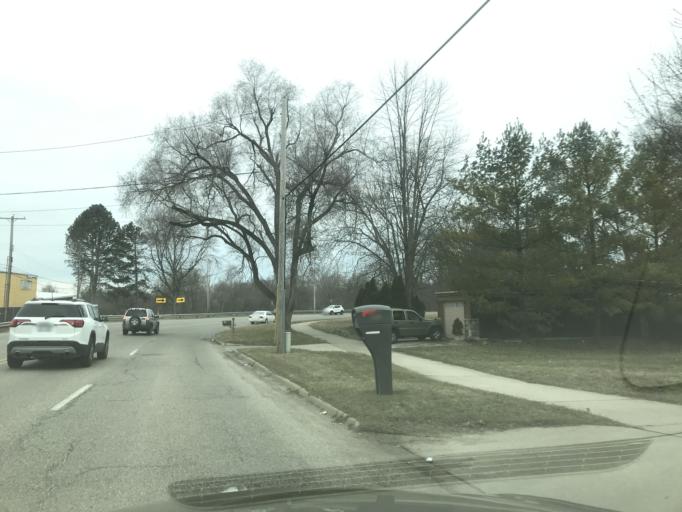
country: US
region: Michigan
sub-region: Ingham County
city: East Lansing
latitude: 42.7552
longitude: -84.4742
